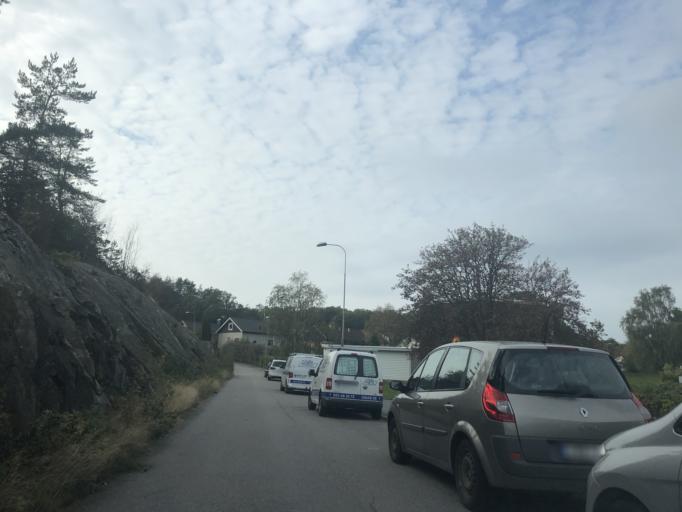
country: SE
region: Vaestra Goetaland
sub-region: Goteborg
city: Majorna
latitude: 57.6600
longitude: 11.8657
